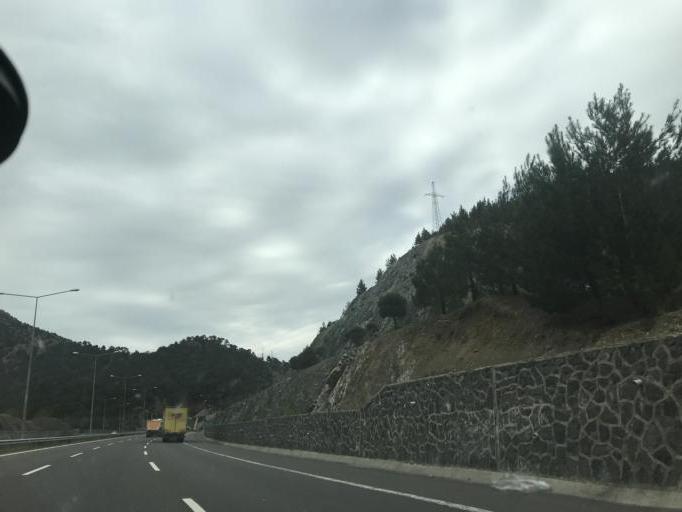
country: TR
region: Nigde
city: Ciftehan
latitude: 37.5039
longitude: 34.8224
